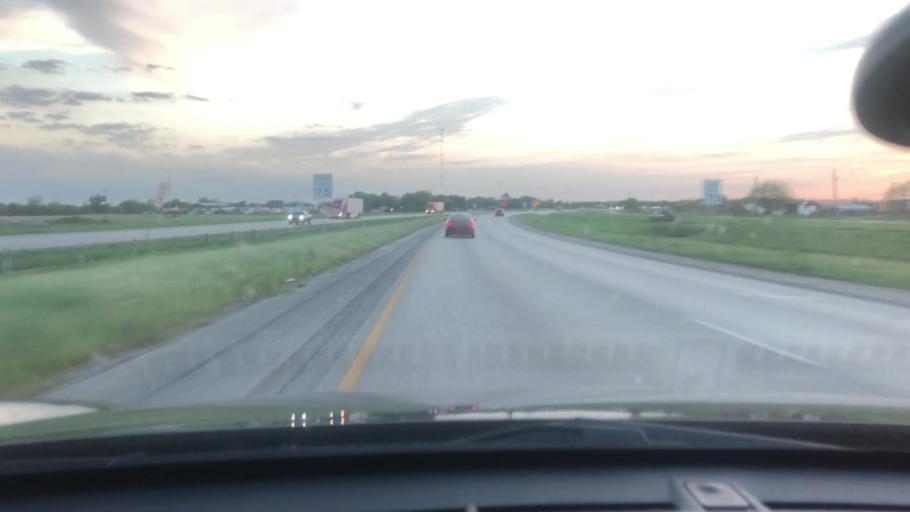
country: US
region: Texas
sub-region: Jackson County
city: Edna
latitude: 28.9671
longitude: -96.6724
